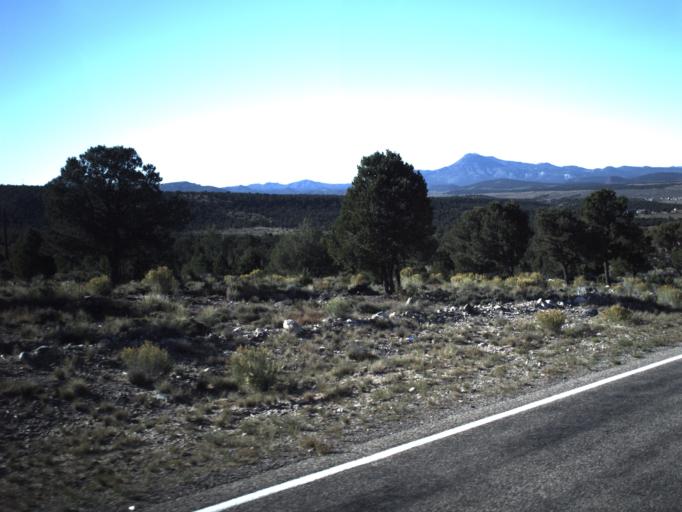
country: US
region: Utah
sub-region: Garfield County
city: Panguitch
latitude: 37.7959
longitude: -112.4371
